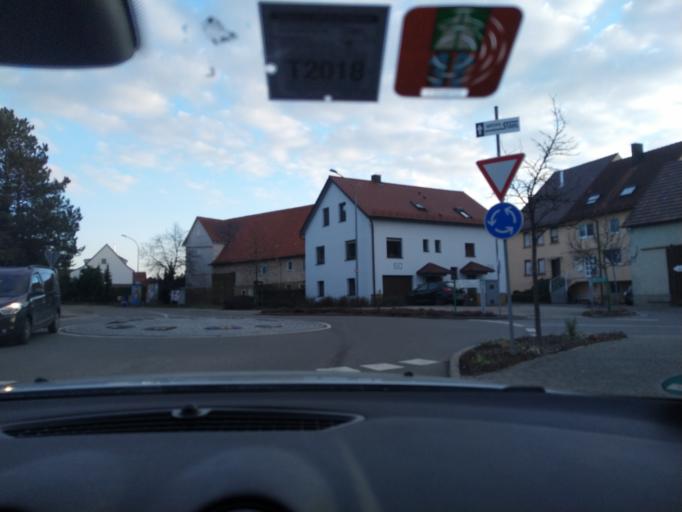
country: DE
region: Baden-Wuerttemberg
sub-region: Regierungsbezirk Stuttgart
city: Neckarwestheim
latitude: 49.0453
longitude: 9.1937
